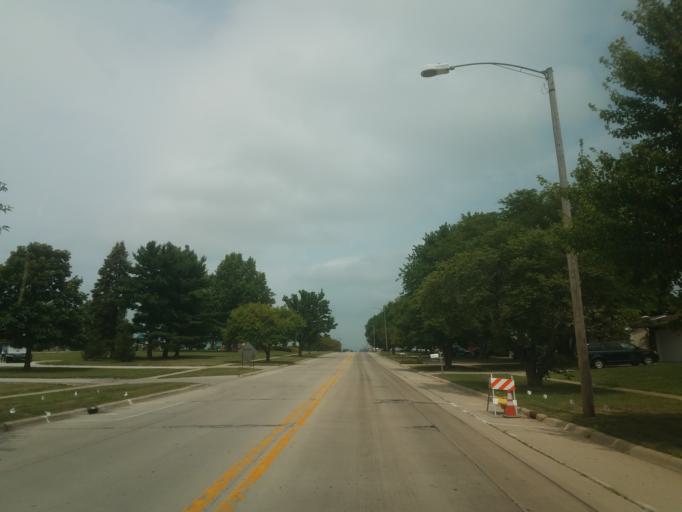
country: US
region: Illinois
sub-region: McLean County
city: Normal
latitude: 40.5144
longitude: -89.0211
